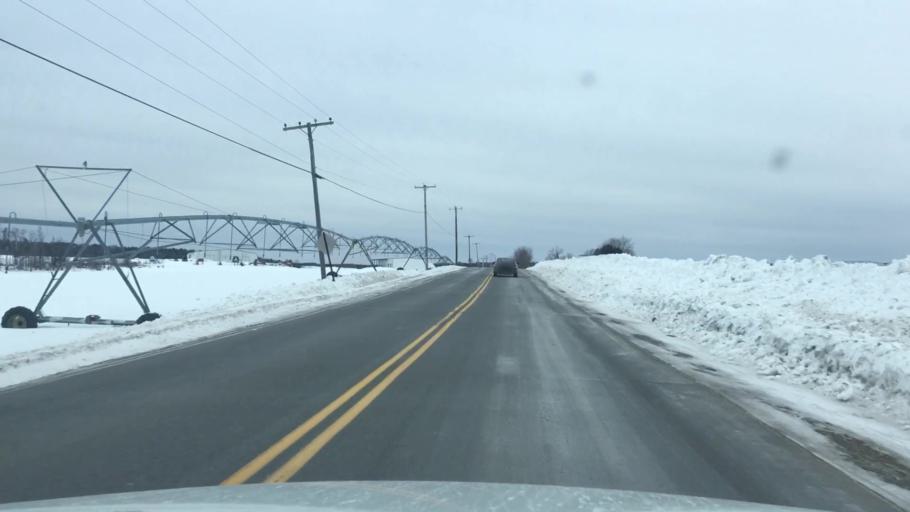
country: US
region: Maine
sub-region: Penobscot County
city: Garland
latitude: 44.9819
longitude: -69.0884
